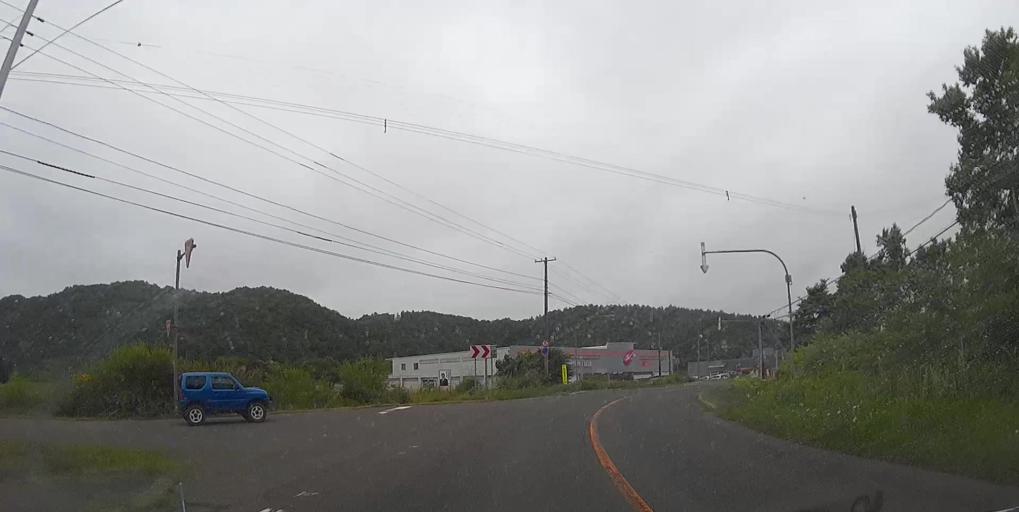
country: JP
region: Hokkaido
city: Iwanai
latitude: 42.4341
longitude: 139.9997
